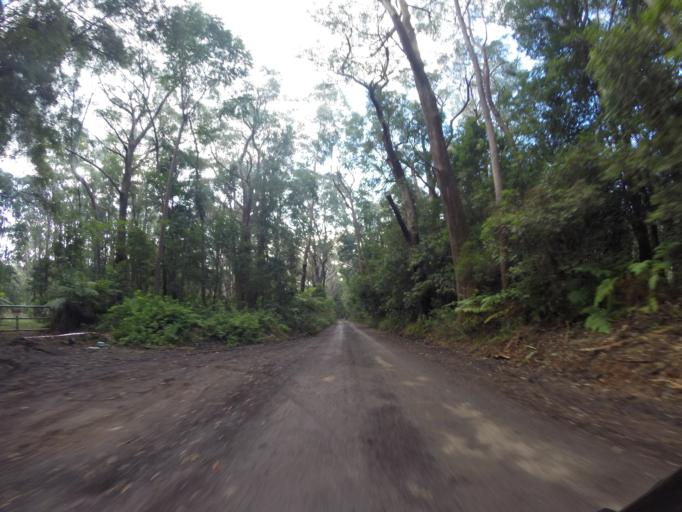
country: AU
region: New South Wales
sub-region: Wollongong
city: Cordeaux Heights
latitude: -34.4261
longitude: 150.7809
